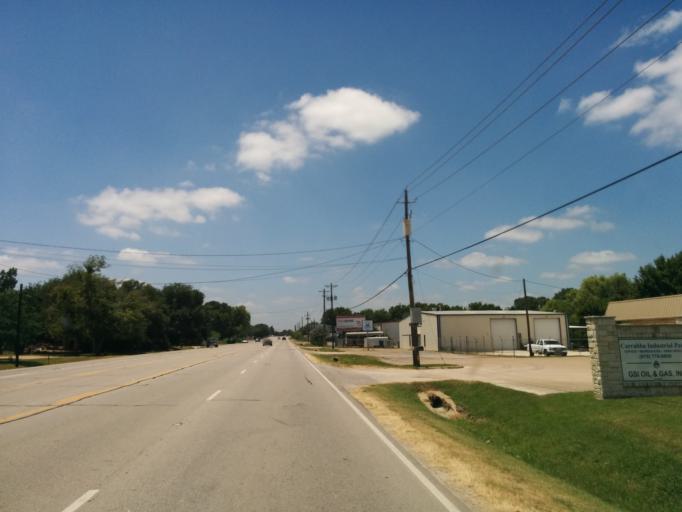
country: US
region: Texas
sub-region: Brazos County
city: Bryan
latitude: 30.7033
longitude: -96.3524
